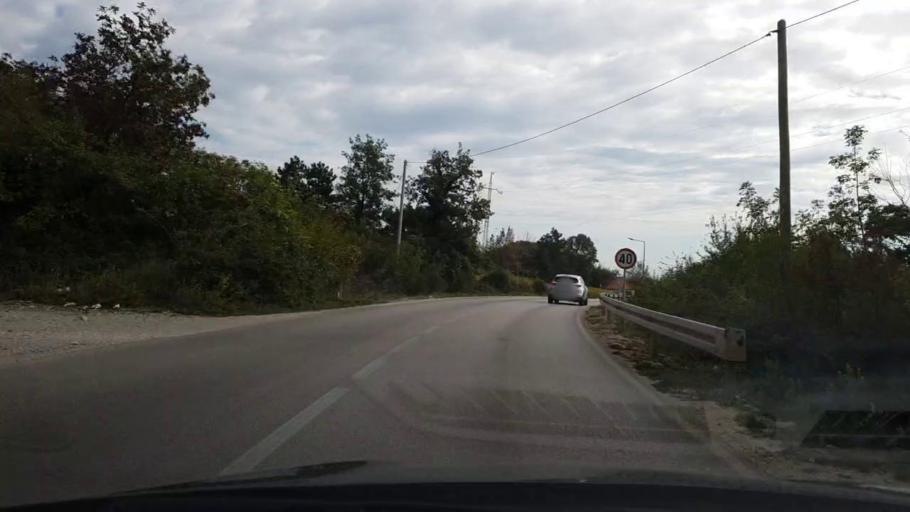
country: ME
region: Herceg Novi
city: Herceg-Novi
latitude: 42.4822
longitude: 18.5285
